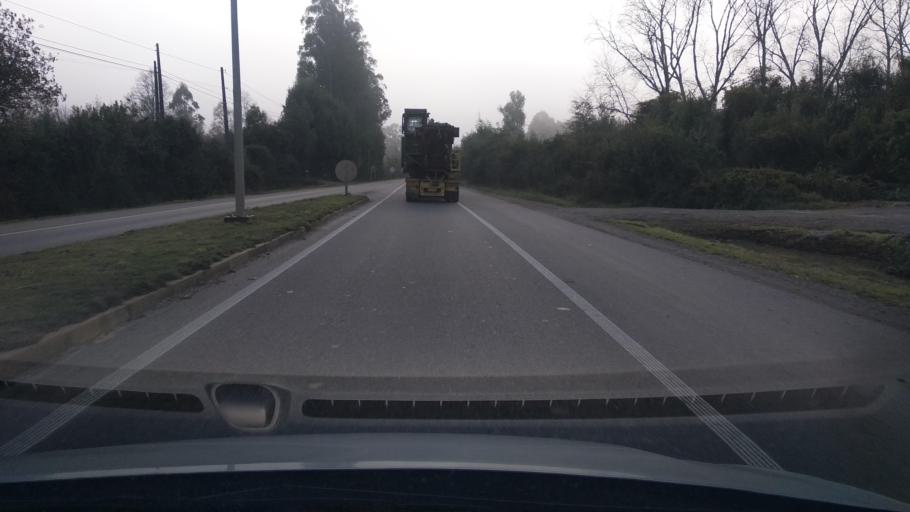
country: CL
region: Los Lagos
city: Las Animas
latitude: -39.7704
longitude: -73.2217
